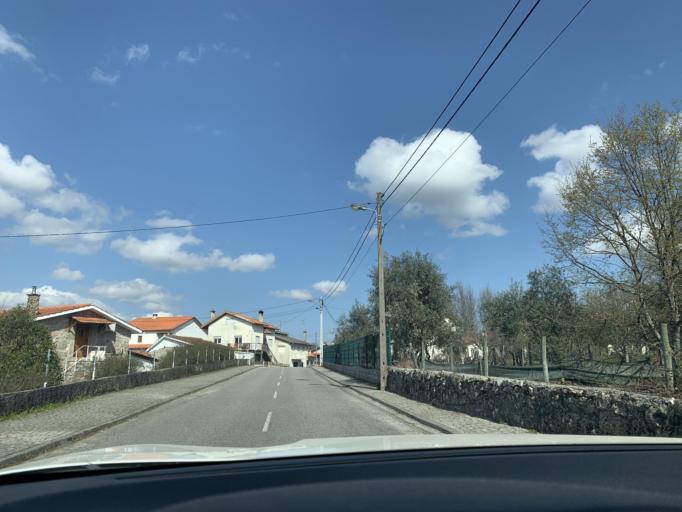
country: PT
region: Viseu
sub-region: Viseu
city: Rio de Loba
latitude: 40.6693
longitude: -7.8792
